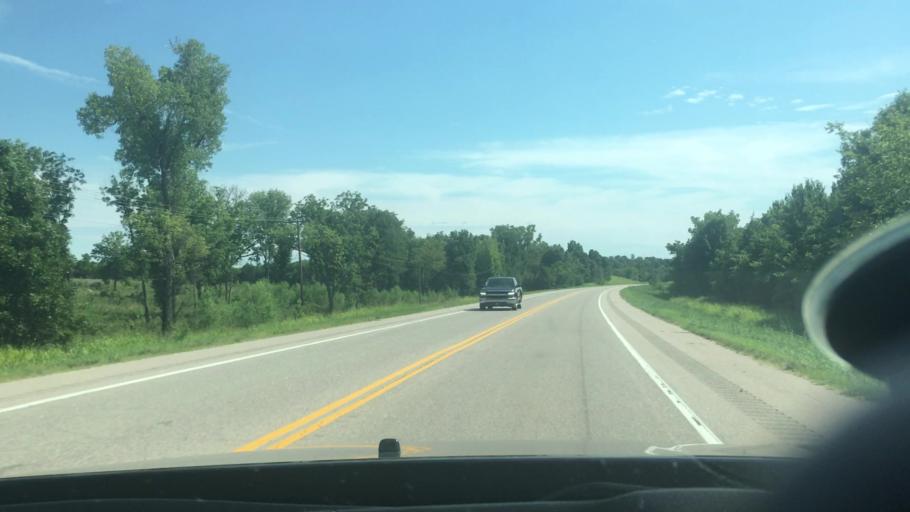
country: US
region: Oklahoma
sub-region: Seminole County
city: Konawa
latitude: 34.9563
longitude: -96.6786
